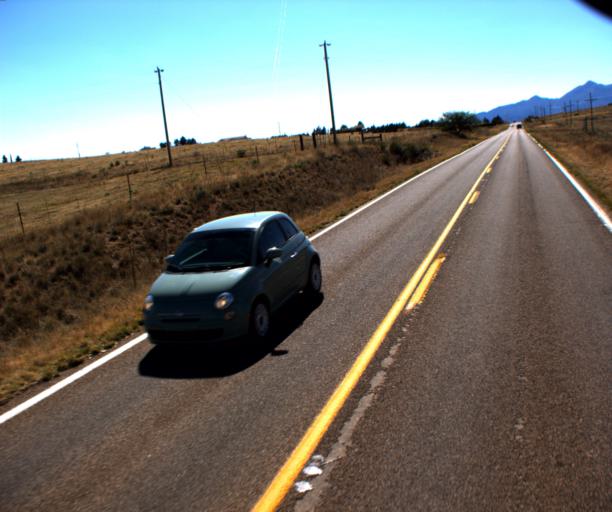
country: US
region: Arizona
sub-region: Cochise County
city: Huachuca City
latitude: 31.6736
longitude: -110.6232
